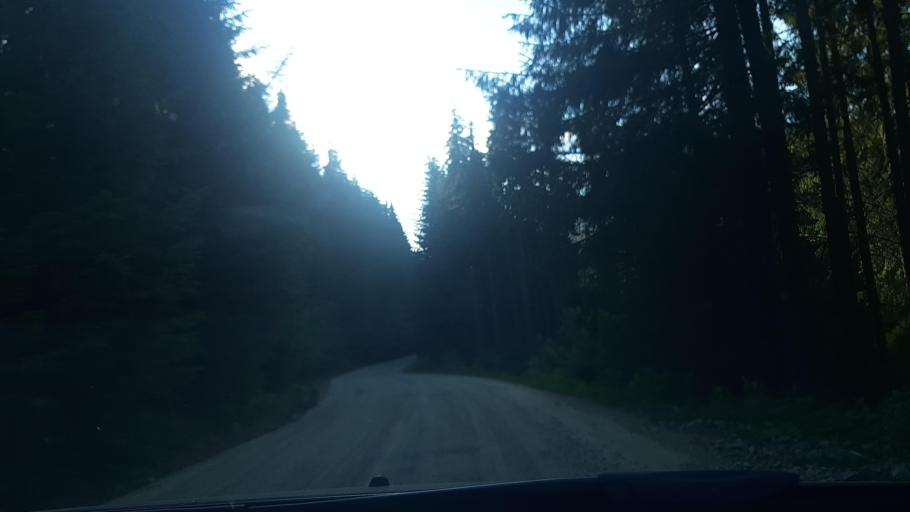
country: RO
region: Alba
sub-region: Comuna Sugag
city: Sugag
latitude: 45.5750
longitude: 23.6098
